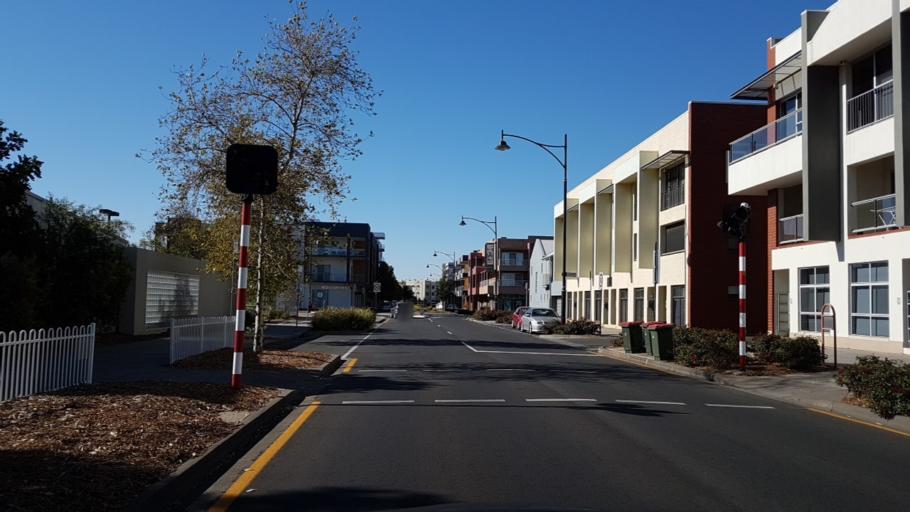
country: AU
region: South Australia
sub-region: Salisbury
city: Ingle Farm
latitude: -34.8089
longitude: 138.6148
